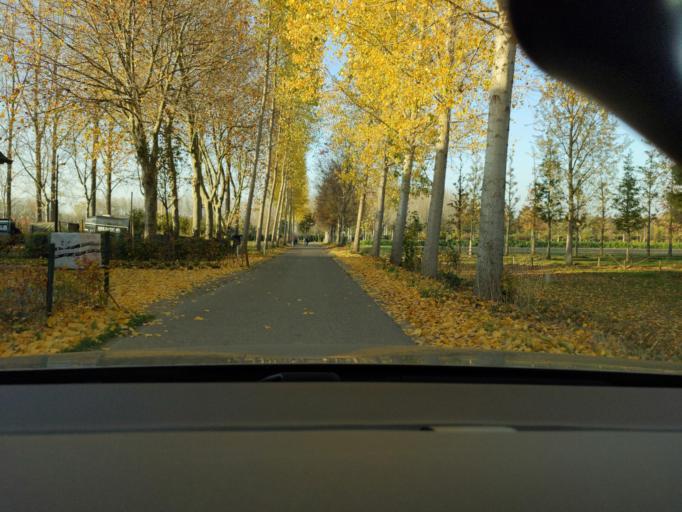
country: NL
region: North Brabant
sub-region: Gemeente Best
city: Best
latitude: 51.5469
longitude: 5.4081
